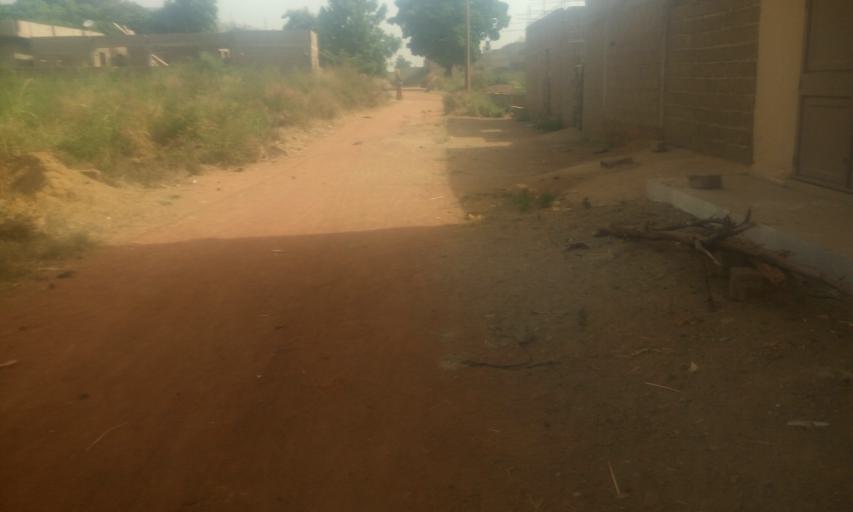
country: ML
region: Bamako
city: Bamako
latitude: 12.5827
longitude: -8.0787
